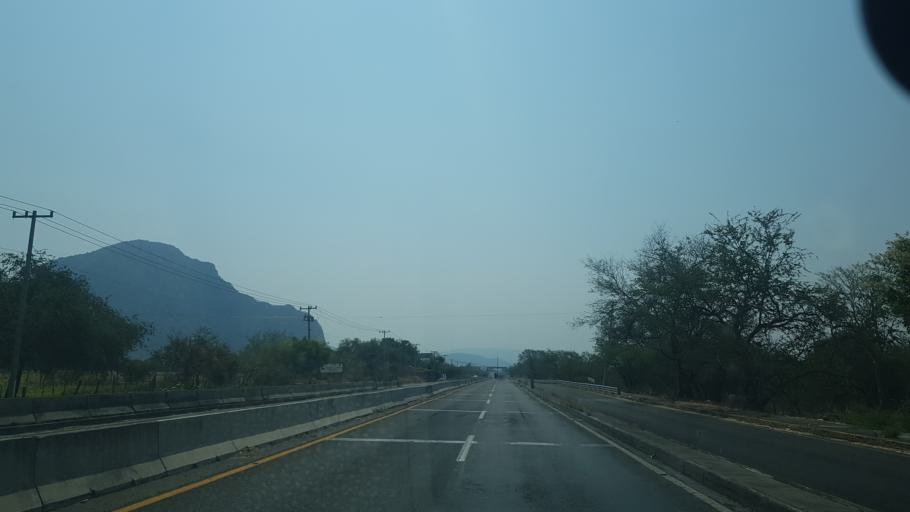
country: MX
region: Morelos
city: Jantetelco
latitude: 18.7090
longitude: -98.7782
